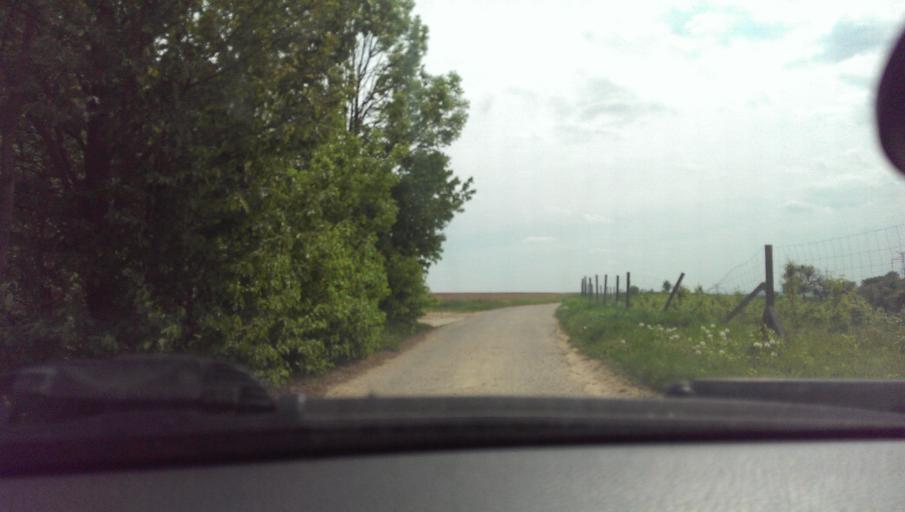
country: CZ
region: Zlin
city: Tlumacov
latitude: 49.2592
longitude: 17.5343
